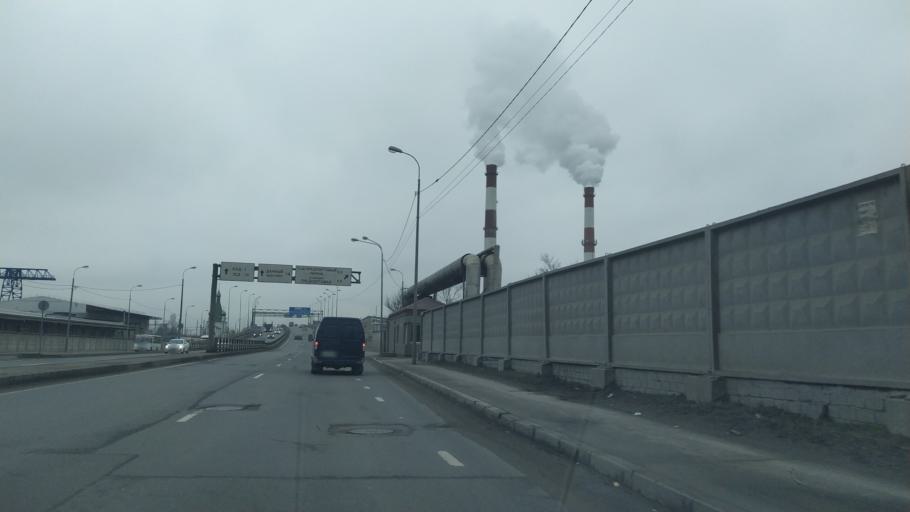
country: RU
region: St.-Petersburg
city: Dachnoye
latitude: 59.8324
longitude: 30.3011
